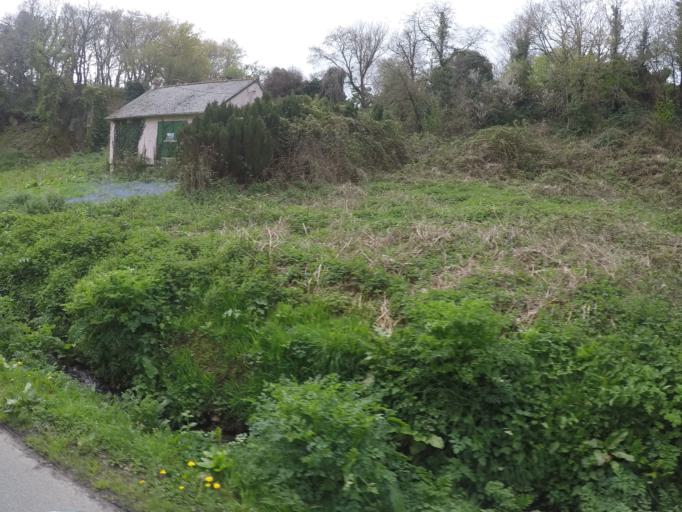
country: FR
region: Brittany
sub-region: Departement des Cotes-d'Armor
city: Plouezec
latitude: 48.7337
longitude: -2.9553
